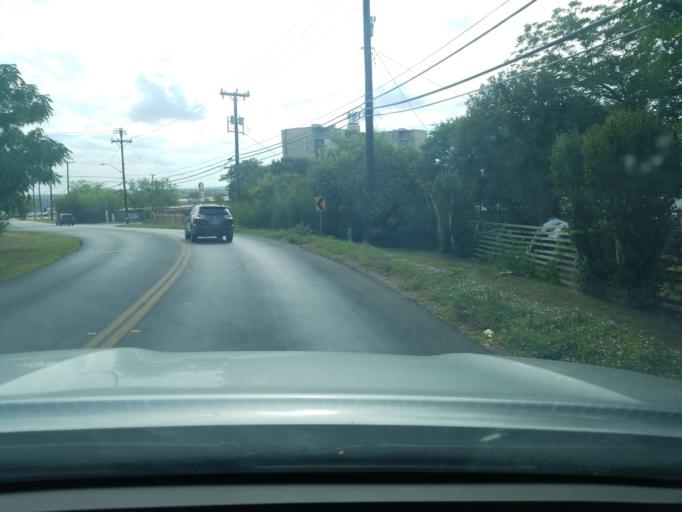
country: US
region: Texas
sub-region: Bexar County
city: Terrell Hills
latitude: 29.4700
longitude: -98.4407
